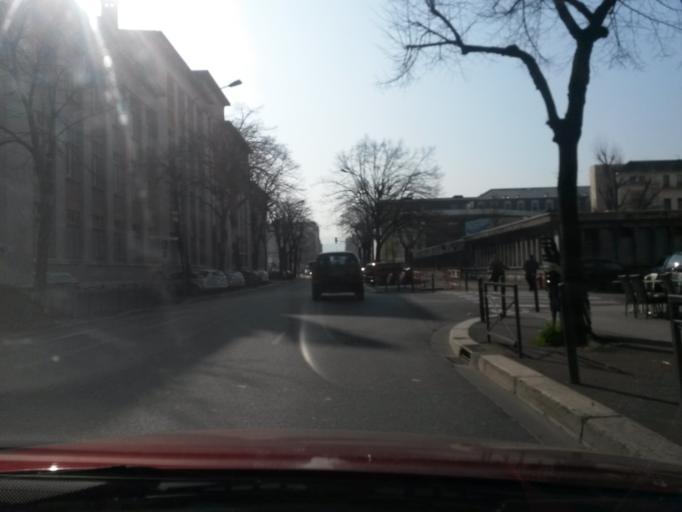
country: FR
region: Rhone-Alpes
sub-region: Departement de l'Isere
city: Saint-Martin-le-Vinoux
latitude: 45.1858
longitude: 5.7249
